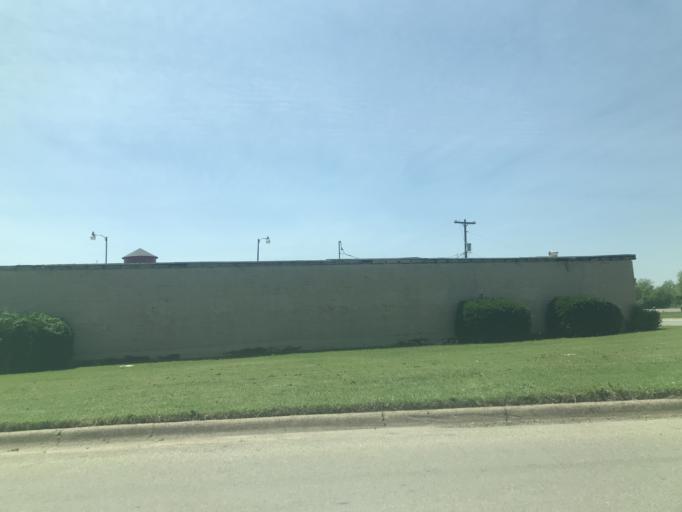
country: US
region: Texas
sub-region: Taylor County
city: Abilene
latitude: 32.4425
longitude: -99.7578
